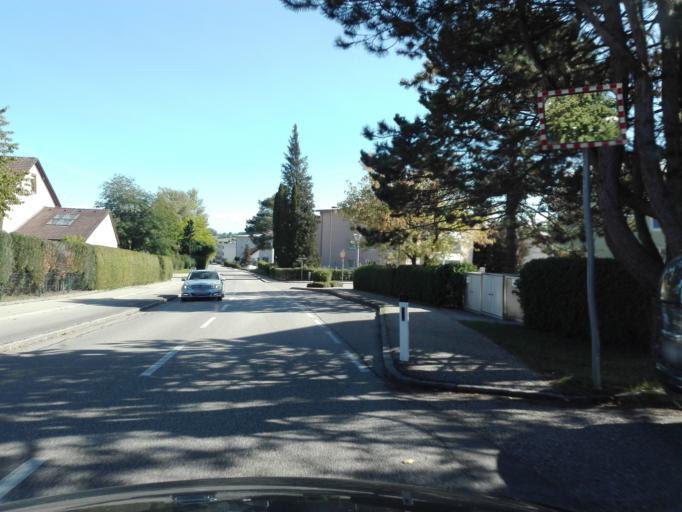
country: AT
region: Upper Austria
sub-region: Politischer Bezirk Linz-Land
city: Sankt Florian
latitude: 48.2043
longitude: 14.3670
